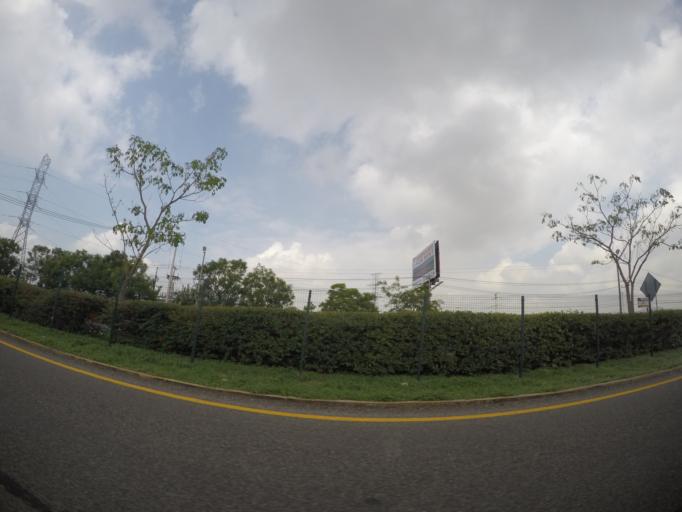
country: MX
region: Jalisco
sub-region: El Salto
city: Las Pintitas
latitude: 20.5704
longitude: -103.3119
